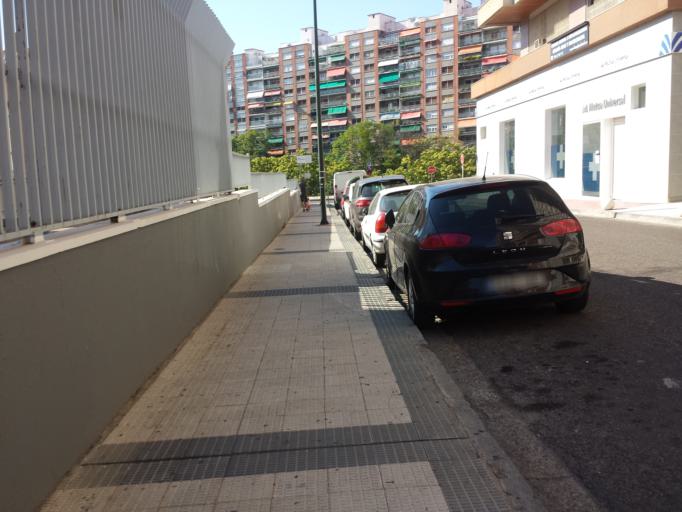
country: ES
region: Aragon
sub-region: Provincia de Zaragoza
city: Delicias
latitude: 41.6368
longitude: -0.8931
